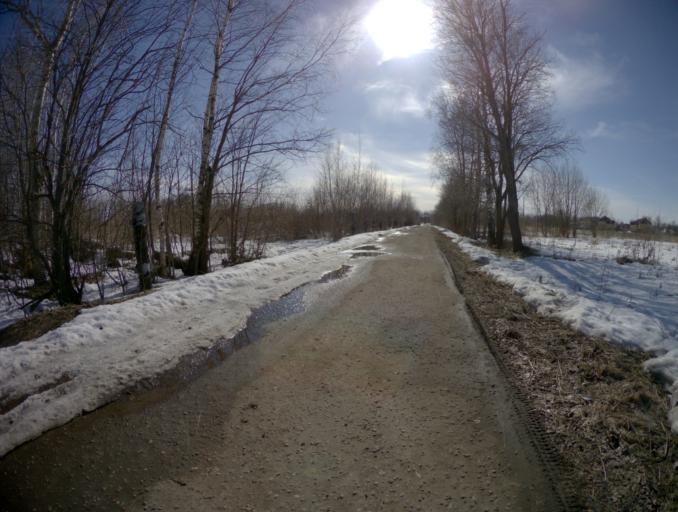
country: RU
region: Vladimir
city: Suzdal'
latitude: 56.4289
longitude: 40.4608
